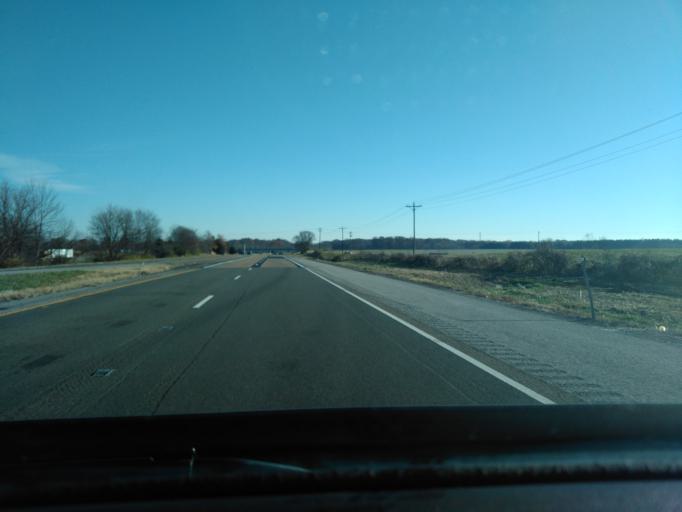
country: US
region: Illinois
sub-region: Madison County
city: Troy
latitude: 38.7513
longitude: -89.9007
